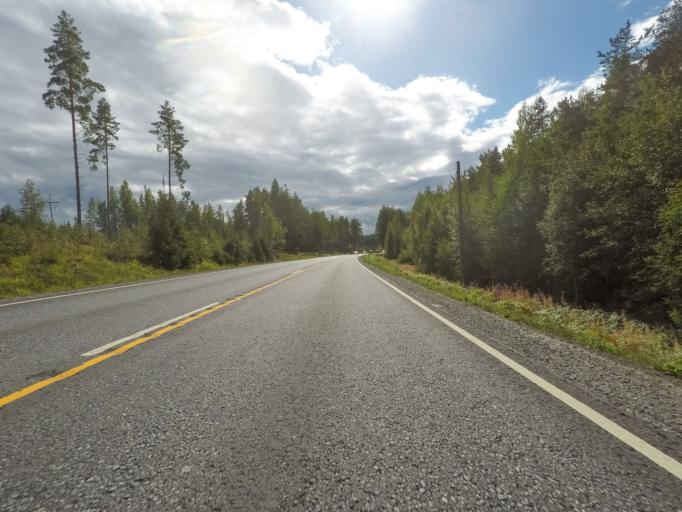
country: FI
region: Paijanne Tavastia
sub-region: Lahti
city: Hartola
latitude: 61.6455
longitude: 26.0277
